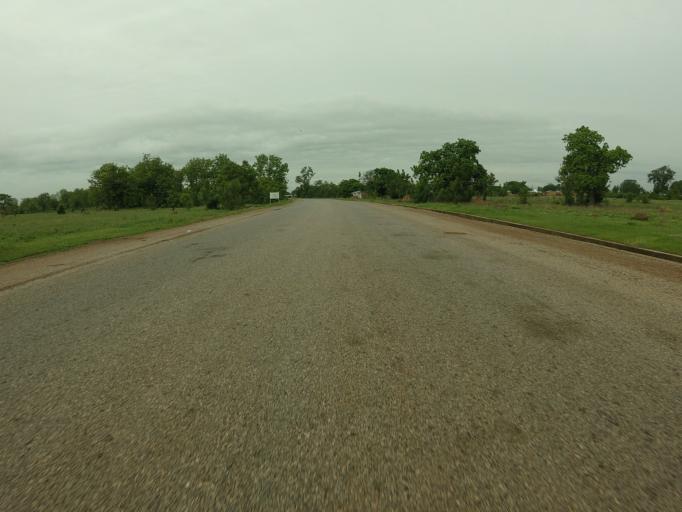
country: GH
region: Northern
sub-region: Yendi
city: Yendi
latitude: 9.5066
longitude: -0.0274
